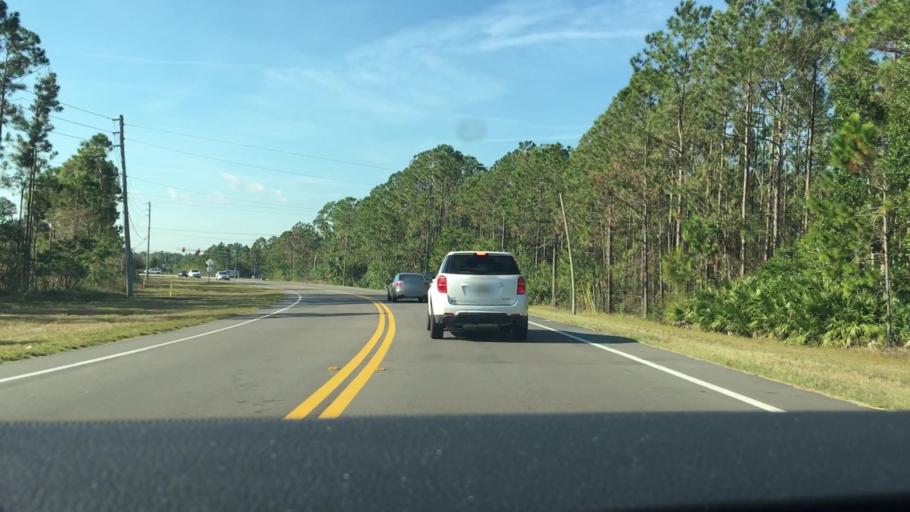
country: US
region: Florida
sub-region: Volusia County
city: Ormond Beach
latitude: 29.2513
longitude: -81.1073
